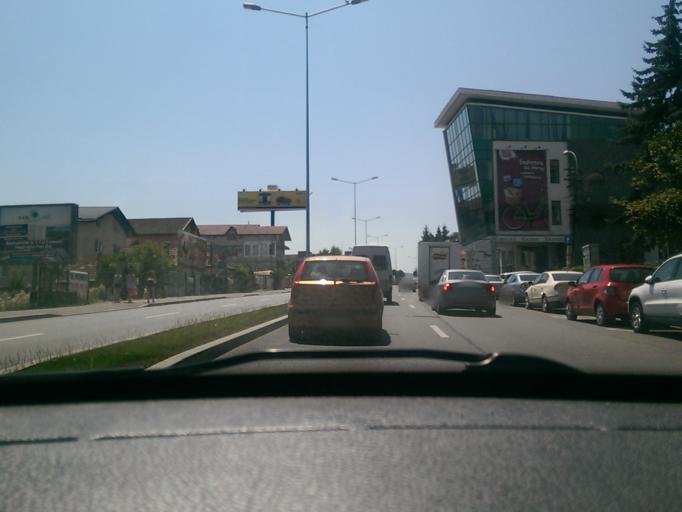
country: RO
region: Cluj
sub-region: Municipiul Cluj-Napoca
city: Cluj-Napoca
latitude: 46.7549
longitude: 23.5960
